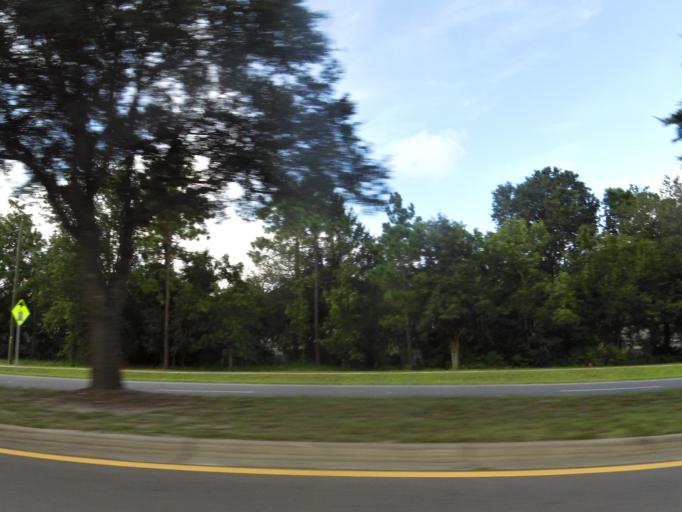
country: US
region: Florida
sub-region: Saint Johns County
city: Fruit Cove
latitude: 30.1109
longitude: -81.5733
